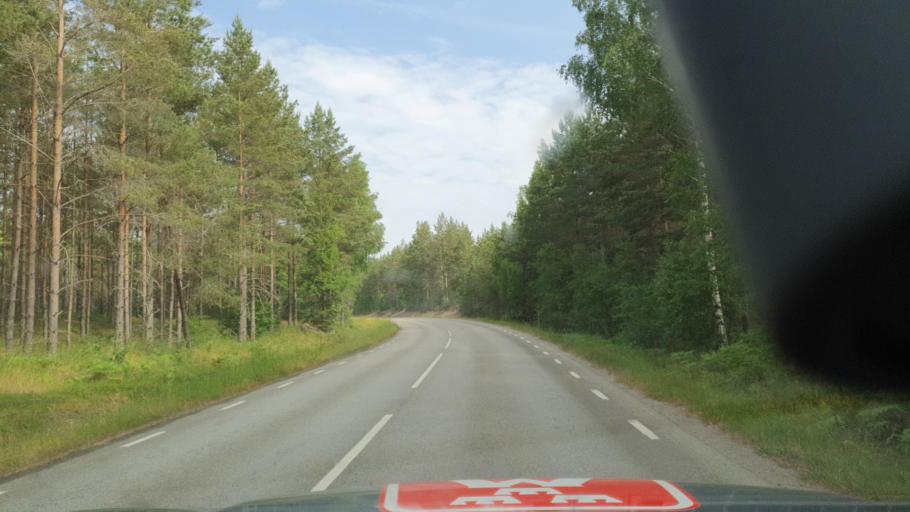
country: SE
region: Kalmar
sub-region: Nybro Kommun
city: Nybro
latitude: 56.6685
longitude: 15.9941
